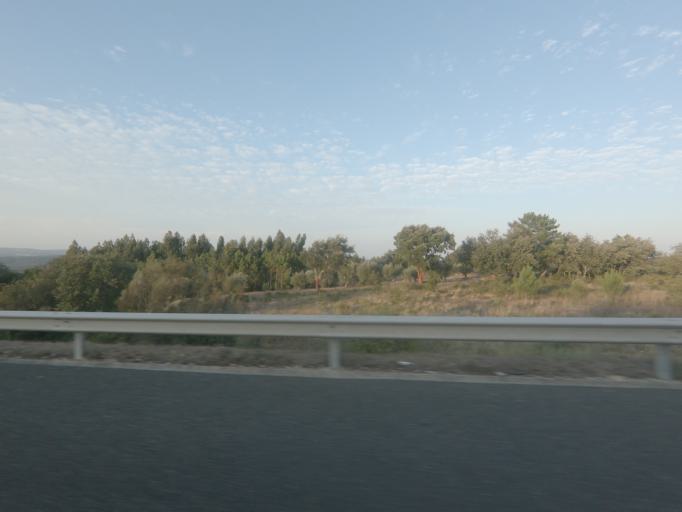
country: PT
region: Leiria
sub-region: Leiria
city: Santa Catarina da Serra
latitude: 39.6876
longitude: -8.6884
